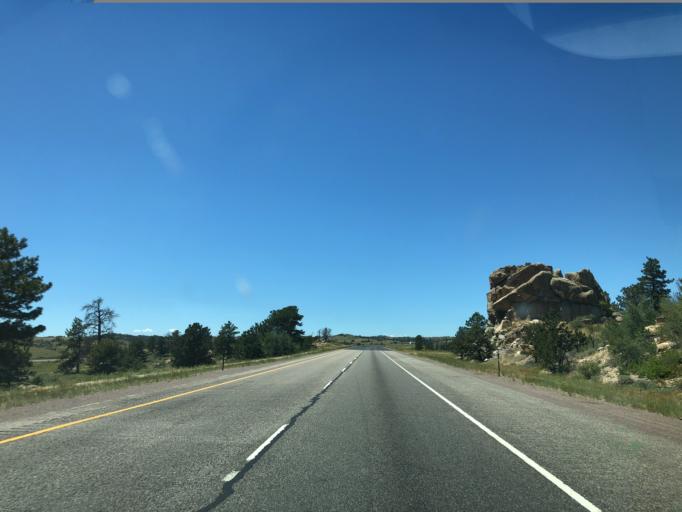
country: US
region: Wyoming
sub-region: Albany County
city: Laramie
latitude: 41.1274
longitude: -105.3302
